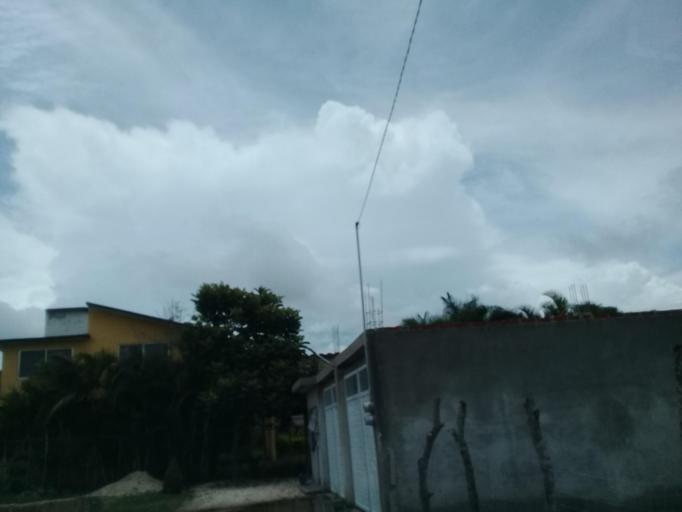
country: MX
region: Veracruz
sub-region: Emiliano Zapata
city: Dos Rios
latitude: 19.4655
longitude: -96.7846
